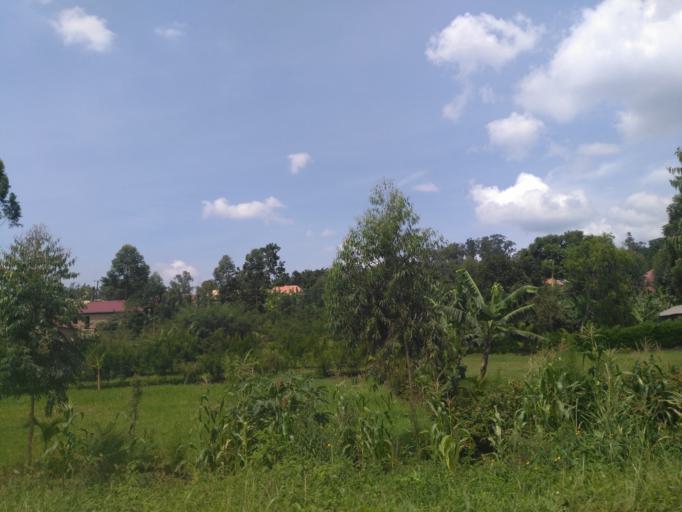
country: UG
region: Central Region
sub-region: Wakiso District
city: Bweyogerere
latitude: 0.4870
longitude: 32.6103
